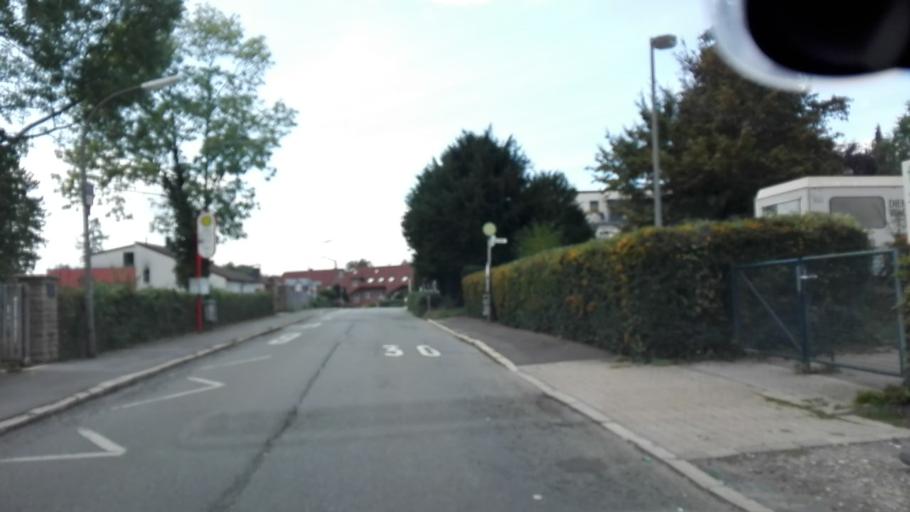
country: DE
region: North Rhine-Westphalia
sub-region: Regierungsbezirk Arnsberg
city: Dortmund
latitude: 51.4909
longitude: 7.4251
